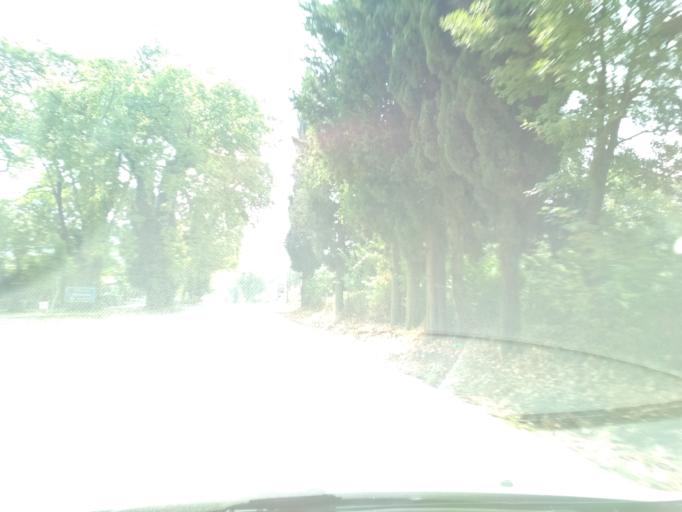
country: GR
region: Central Greece
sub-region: Nomos Evvoias
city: Prokopion
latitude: 38.7242
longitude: 23.5069
